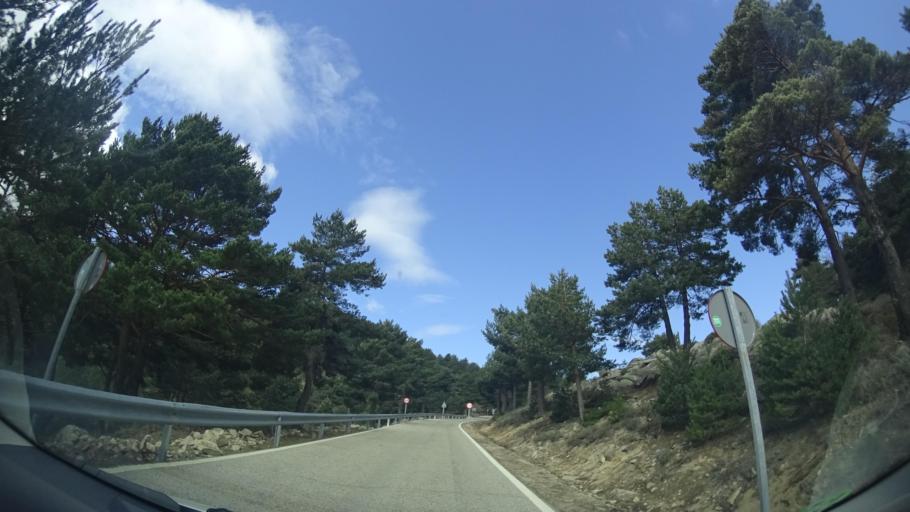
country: ES
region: Madrid
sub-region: Provincia de Madrid
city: Canencia
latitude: 40.8668
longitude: -3.7618
